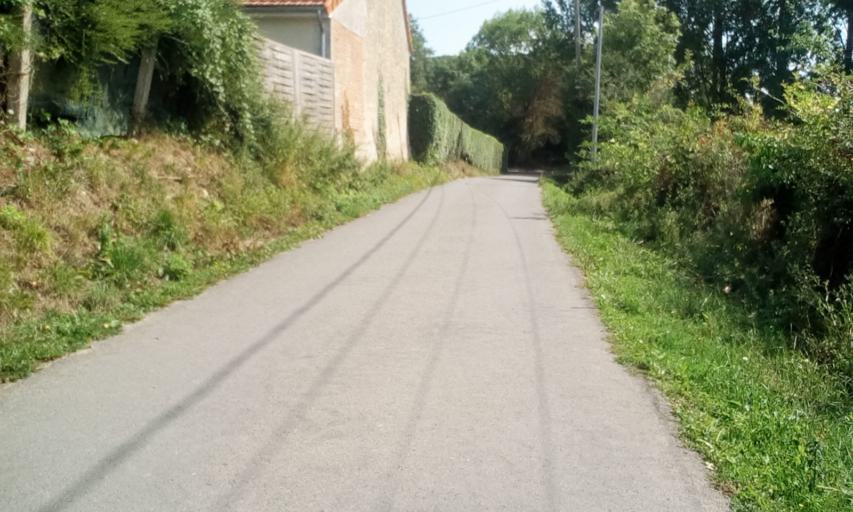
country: FR
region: Lower Normandy
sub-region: Departement du Calvados
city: Argences
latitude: 49.1261
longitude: -0.1581
